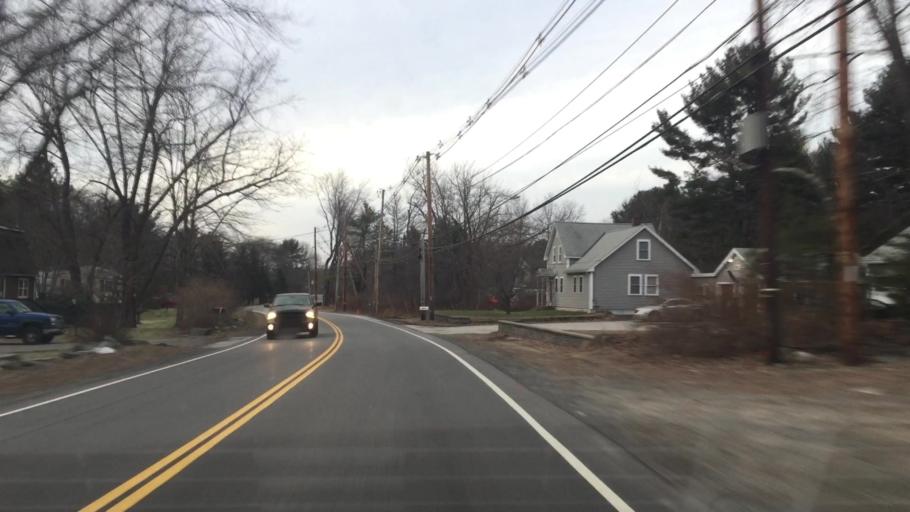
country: US
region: New Hampshire
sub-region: Hillsborough County
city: Pelham
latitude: 42.7440
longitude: -71.2907
